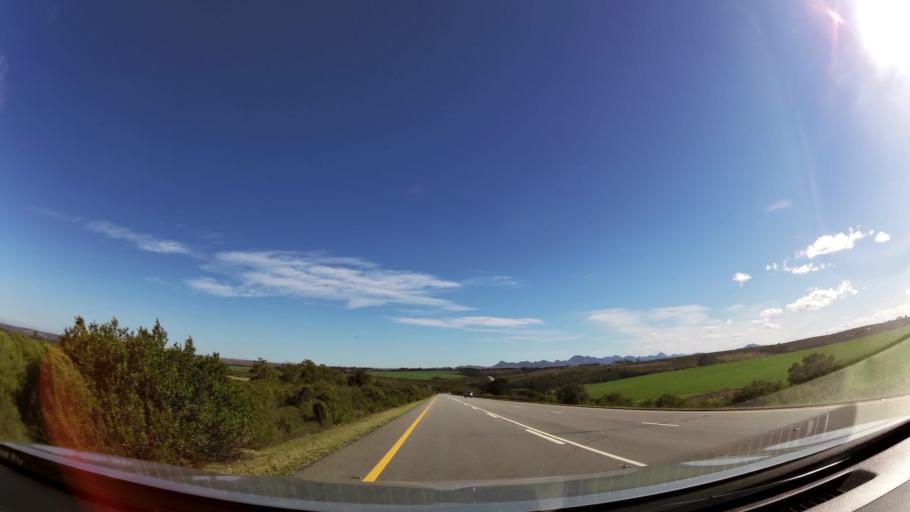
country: ZA
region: Eastern Cape
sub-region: Cacadu District Municipality
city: Kruisfontein
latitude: -34.0115
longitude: 24.6476
